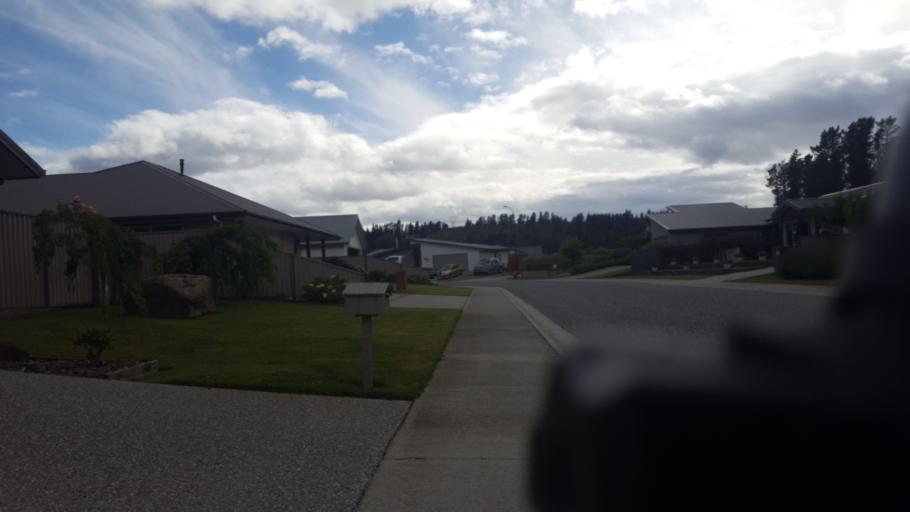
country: NZ
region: Otago
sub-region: Queenstown-Lakes District
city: Wanaka
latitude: -45.2404
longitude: 169.3815
